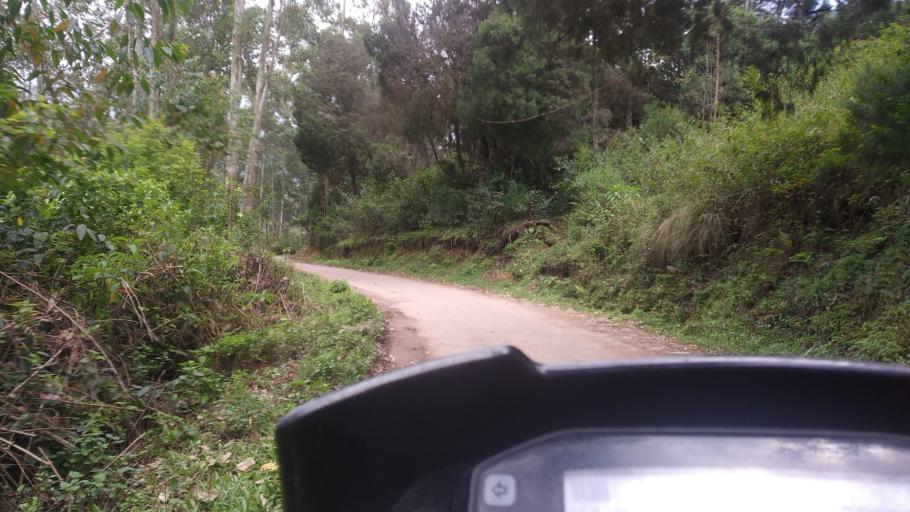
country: IN
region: Kerala
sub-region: Idukki
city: Munnar
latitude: 10.0558
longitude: 77.1094
